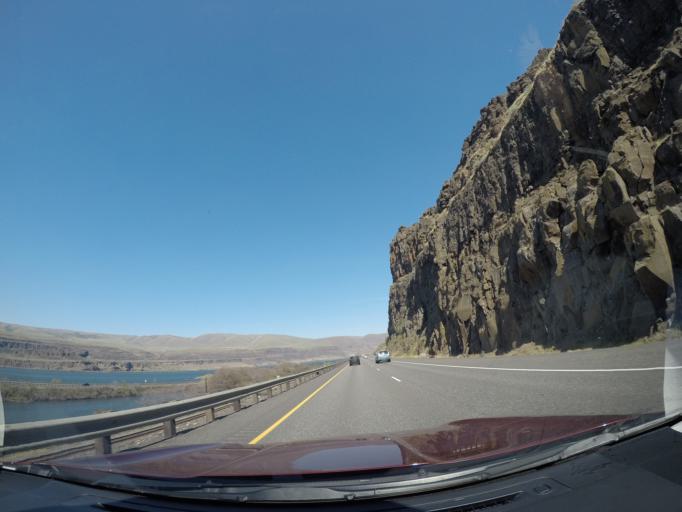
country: US
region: Washington
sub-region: Klickitat County
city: Dallesport
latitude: 45.6346
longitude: -121.0957
